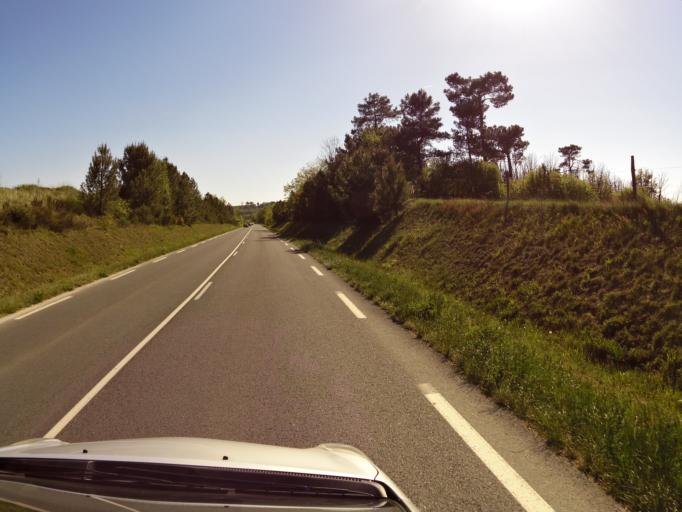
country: FR
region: Aquitaine
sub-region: Departement de la Dordogne
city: Sarlat-la-Caneda
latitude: 44.9564
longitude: 1.2280
